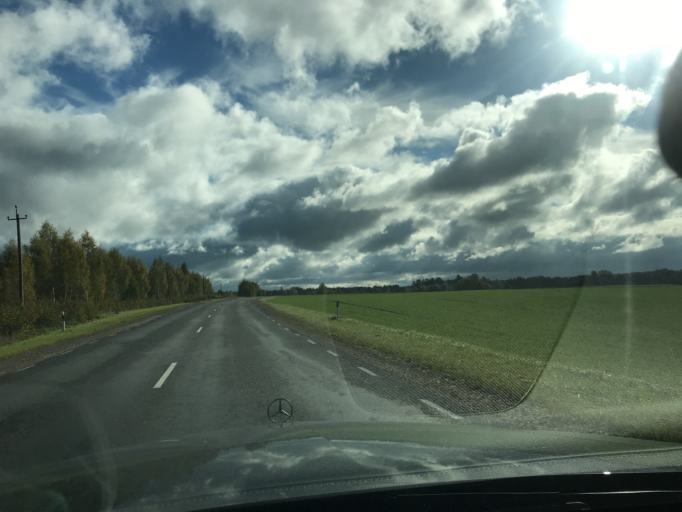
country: EE
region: Tartu
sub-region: Elva linn
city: Elva
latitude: 58.0077
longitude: 26.2563
